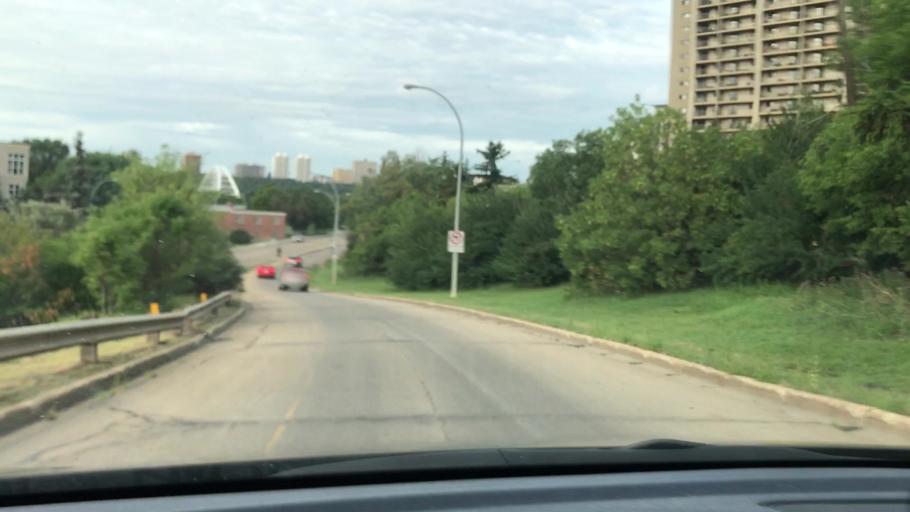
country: CA
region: Alberta
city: Edmonton
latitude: 53.5368
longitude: -113.4945
